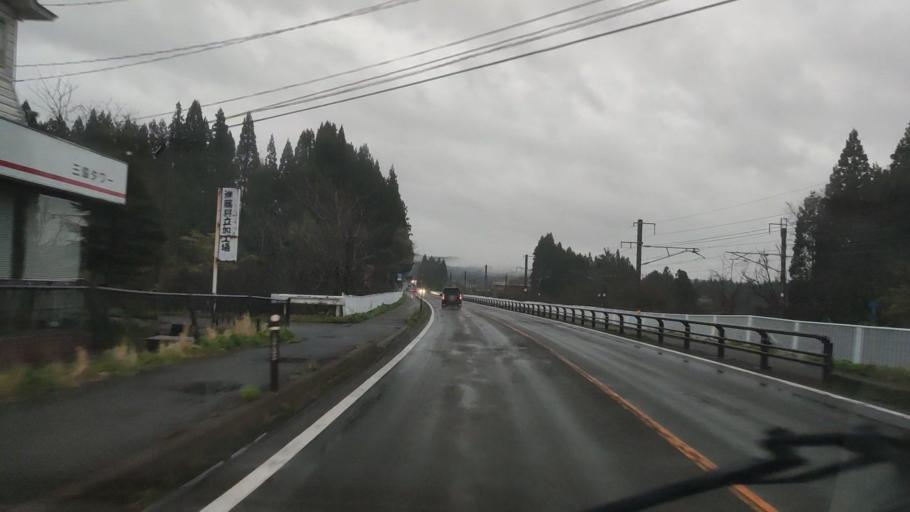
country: JP
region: Akita
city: Omagari
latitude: 39.6117
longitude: 140.3259
